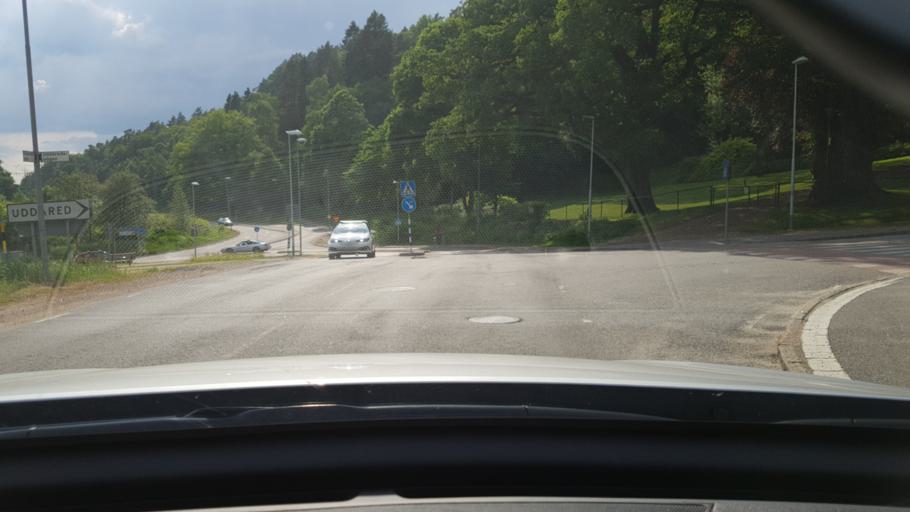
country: SE
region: Vaestra Goetaland
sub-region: Lerums Kommun
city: Stenkullen
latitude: 57.8089
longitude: 12.3582
